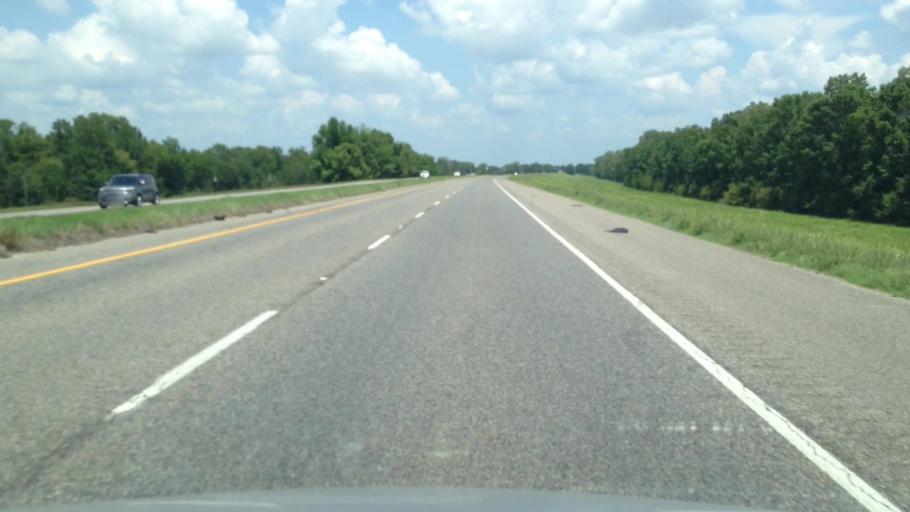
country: US
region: Louisiana
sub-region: Saint Landry Parish
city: Krotz Springs
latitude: 30.5485
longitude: -91.8523
